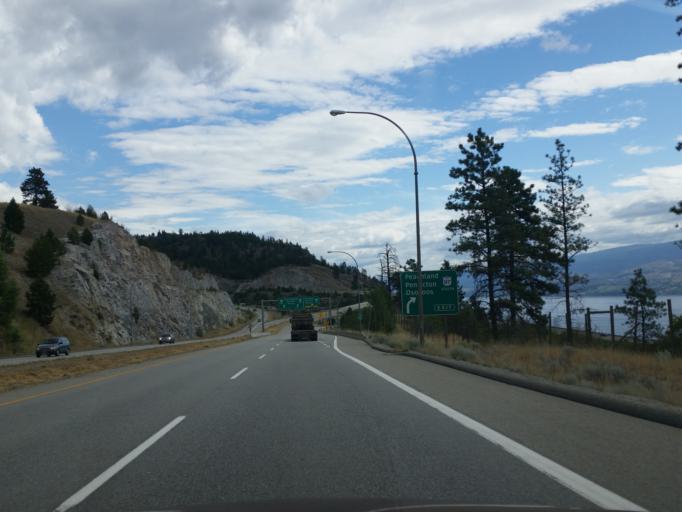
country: CA
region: British Columbia
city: Peachland
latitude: 49.8035
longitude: -119.6729
